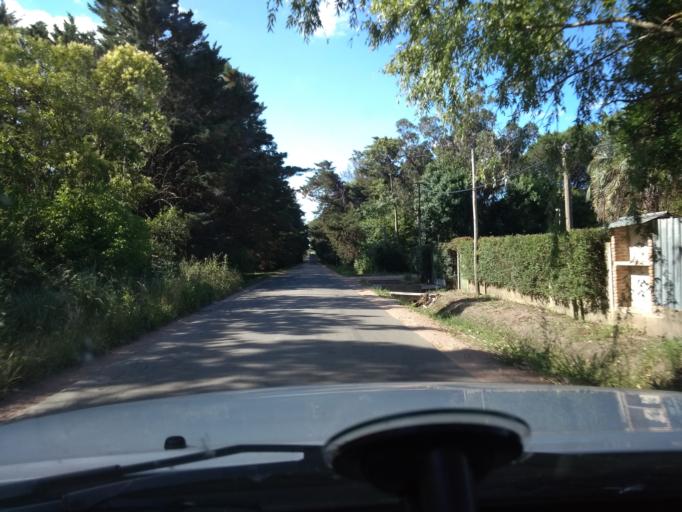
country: UY
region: Canelones
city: La Paz
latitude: -34.7988
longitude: -56.2107
